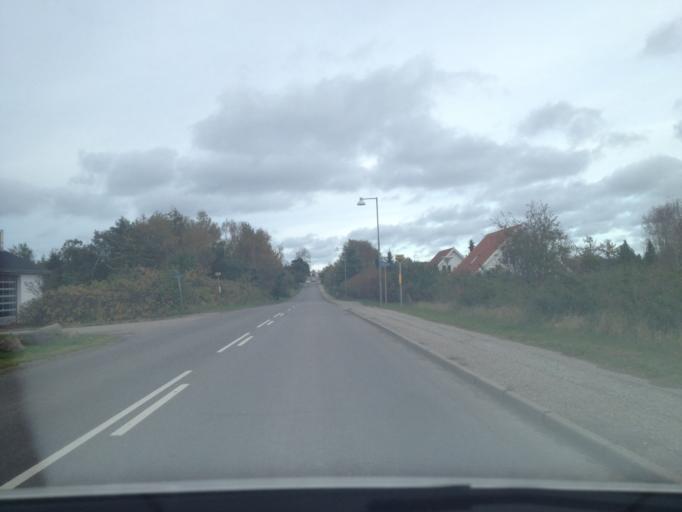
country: DK
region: Zealand
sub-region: Odsherred Kommune
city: Hojby
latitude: 55.9082
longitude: 11.5866
